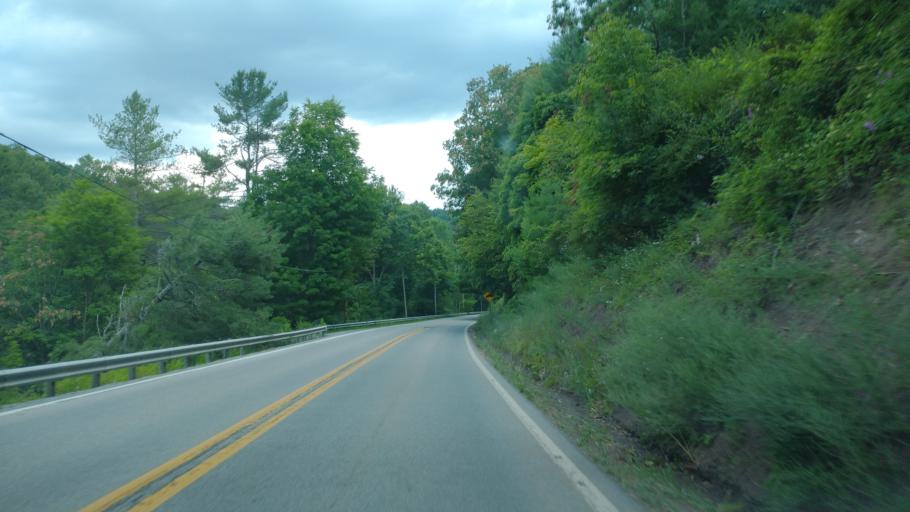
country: US
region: West Virginia
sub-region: Mercer County
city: Athens
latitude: 37.4397
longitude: -81.0027
